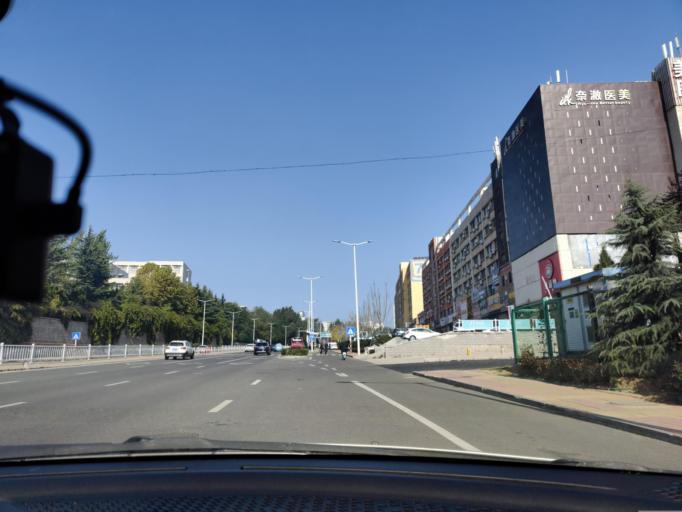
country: CN
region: Shandong Sheng
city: Shihuiyao
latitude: 37.5185
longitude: 121.3585
